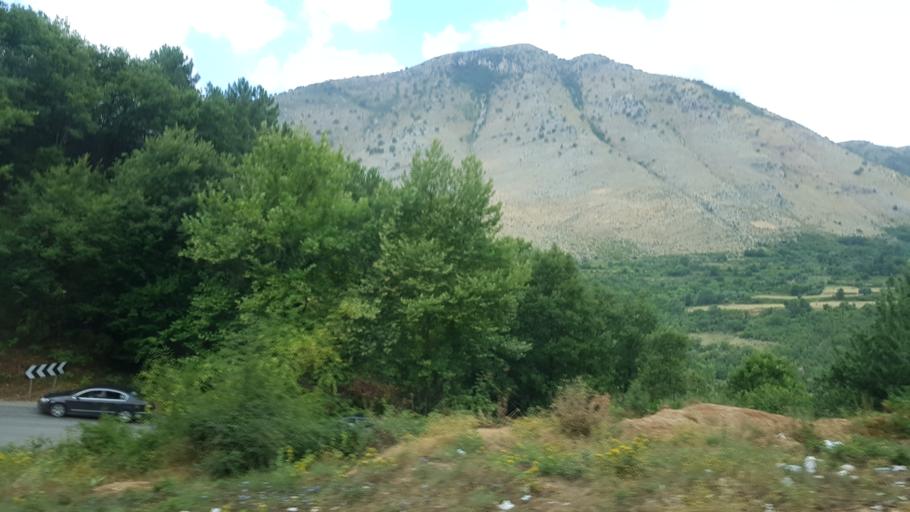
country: AL
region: Vlore
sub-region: Rrethi i Sarandes
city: Dhiver
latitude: 39.9120
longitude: 20.1912
